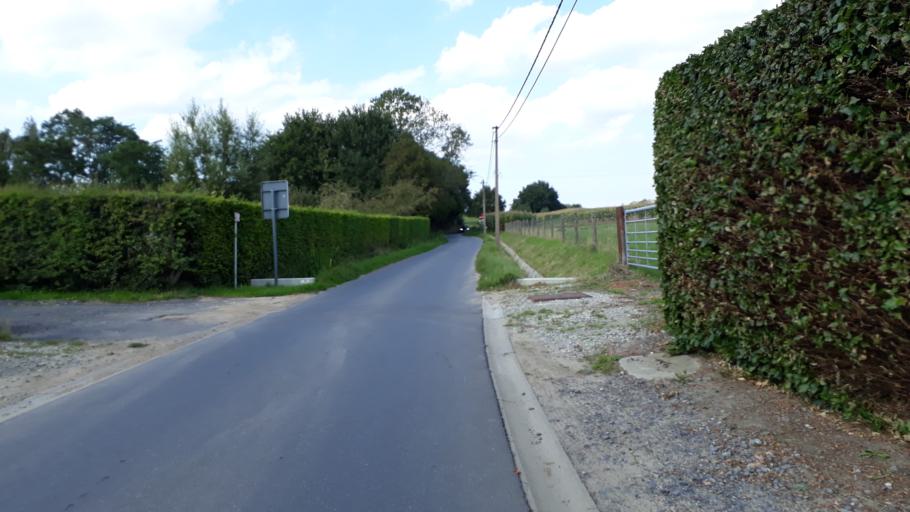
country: BE
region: Flanders
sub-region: Provincie West-Vlaanderen
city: Torhout
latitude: 51.0746
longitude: 3.0810
